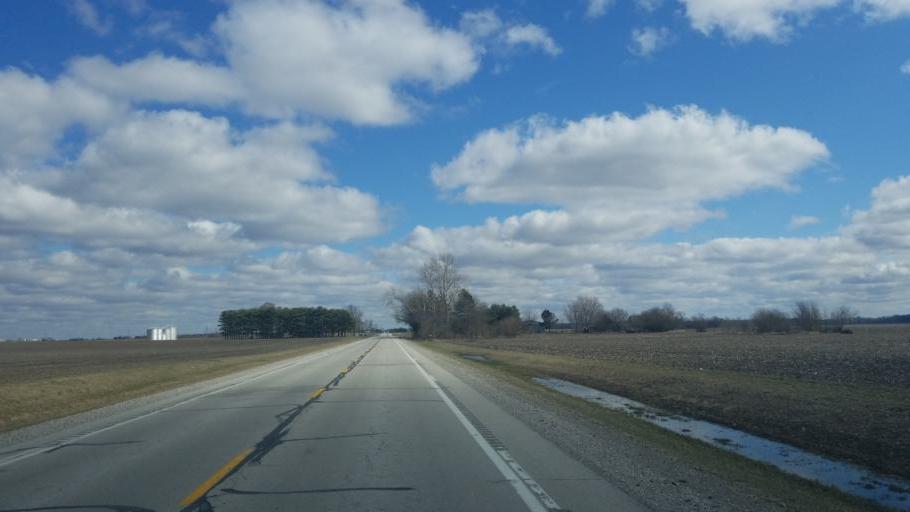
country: US
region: Illinois
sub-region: Douglas County
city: Villa Grove
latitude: 39.7921
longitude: -88.0395
